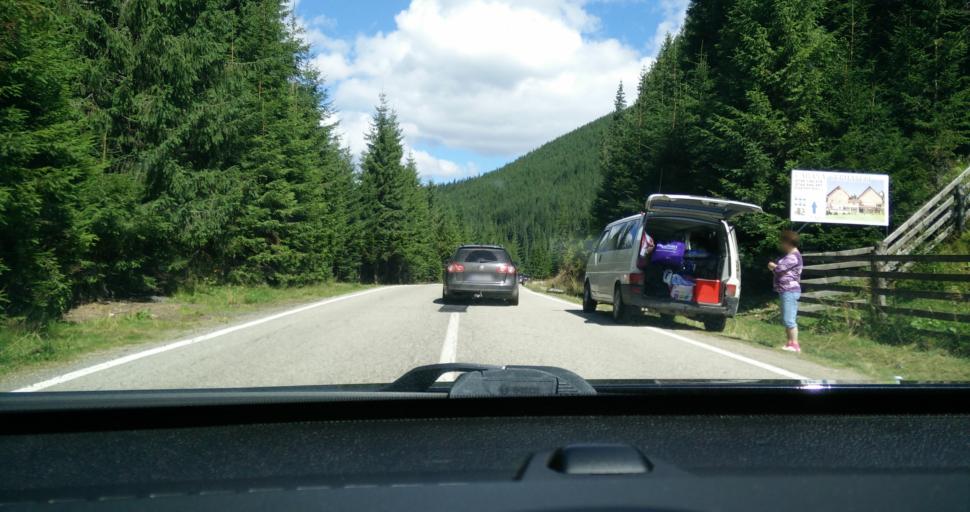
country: RO
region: Alba
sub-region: Comuna Sugag
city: Sugag
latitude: 45.5411
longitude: 23.6381
